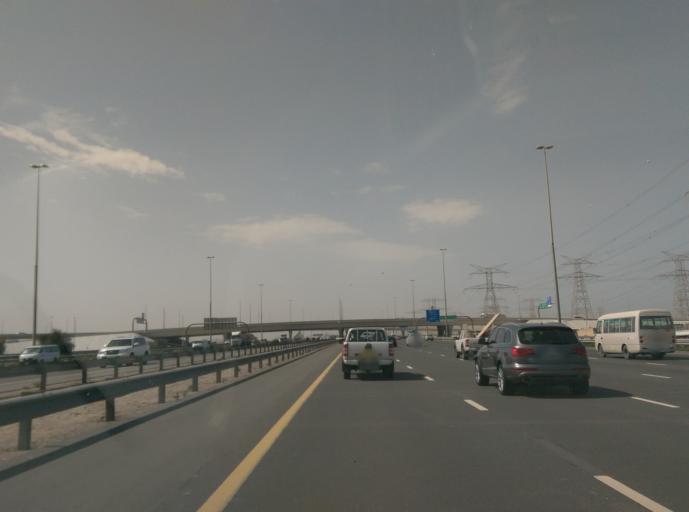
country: AE
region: Dubai
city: Dubai
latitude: 25.1220
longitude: 55.2506
